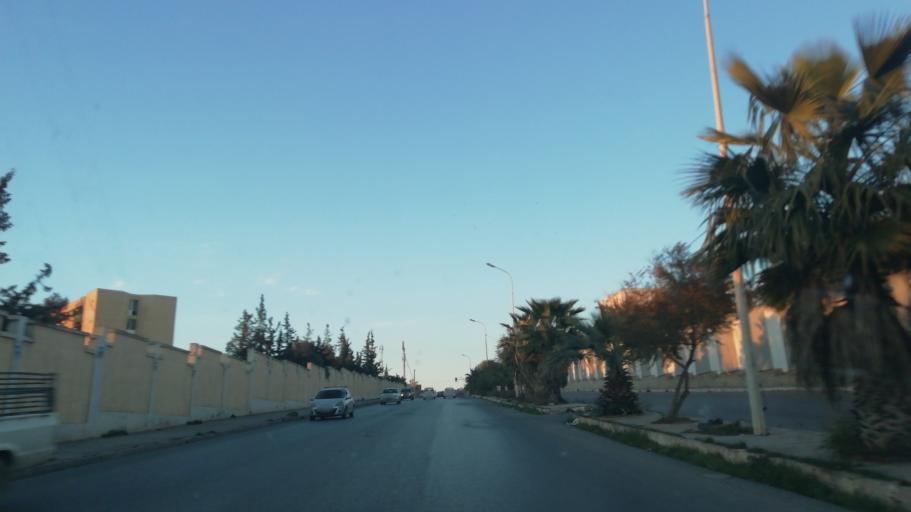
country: DZ
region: Oran
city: Bir el Djir
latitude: 35.7003
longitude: -0.5853
